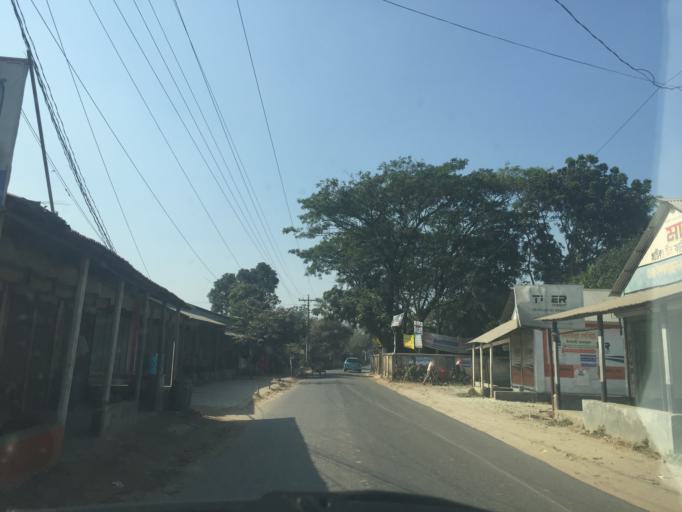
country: BD
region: Dhaka
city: Tungi
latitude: 23.8580
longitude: 90.3209
